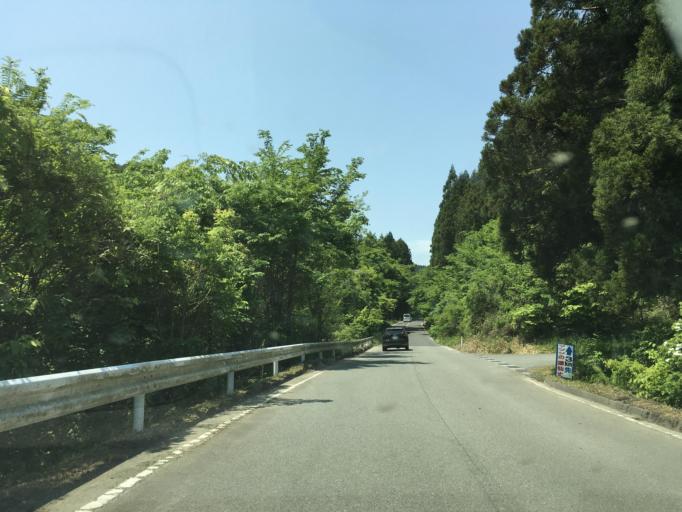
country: JP
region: Iwate
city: Ofunato
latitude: 38.8523
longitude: 141.4958
